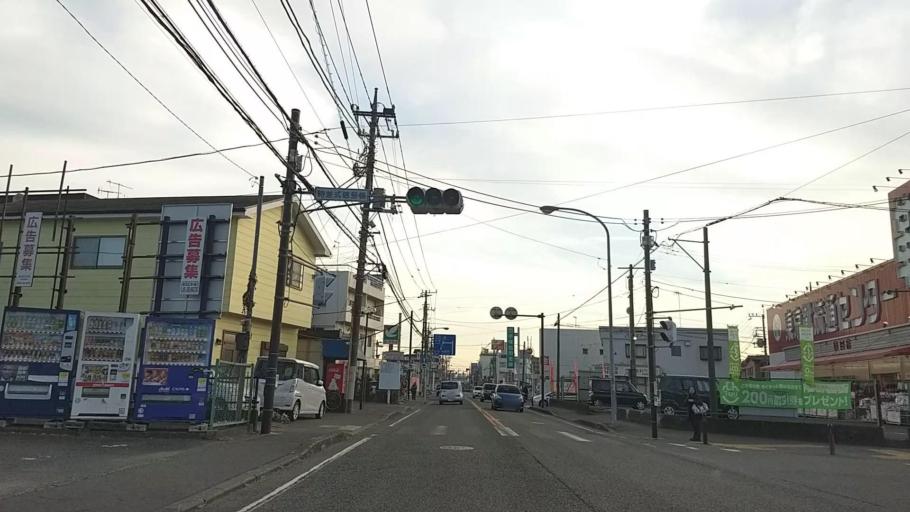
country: JP
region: Kanagawa
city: Atsugi
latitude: 35.4622
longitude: 139.3573
